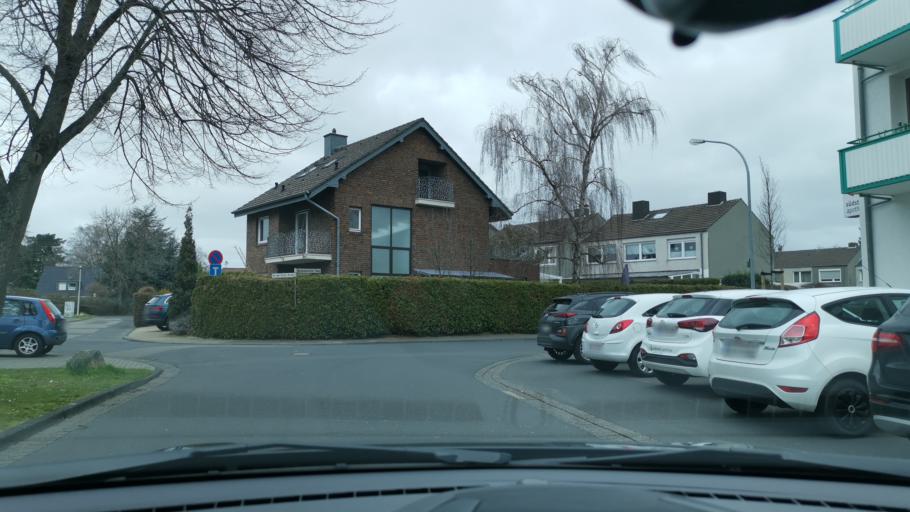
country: DE
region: North Rhine-Westphalia
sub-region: Regierungsbezirk Dusseldorf
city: Grevenbroich
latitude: 51.0836
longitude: 6.6009
